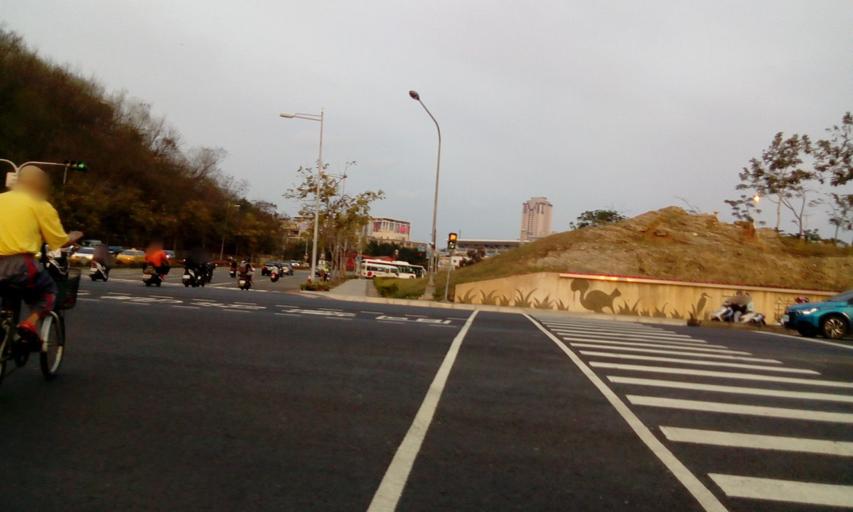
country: TW
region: Kaohsiung
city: Kaohsiung
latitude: 22.6887
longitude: 120.3024
